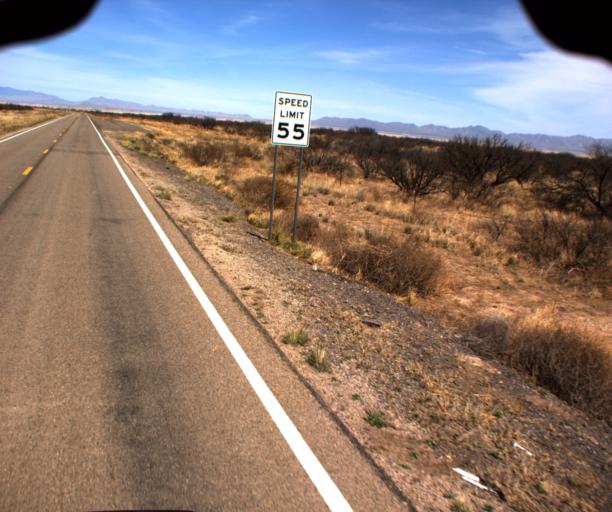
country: US
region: Arizona
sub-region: Cochise County
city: Willcox
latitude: 32.1224
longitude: -109.9098
